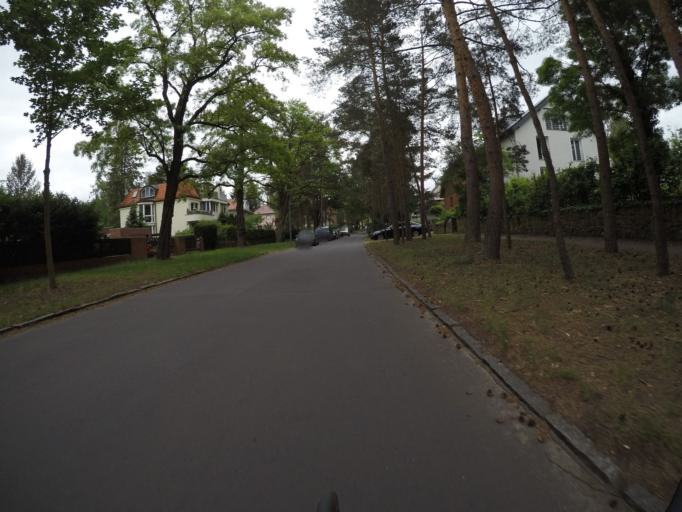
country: DE
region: Berlin
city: Frohnau
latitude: 52.6275
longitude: 13.2721
